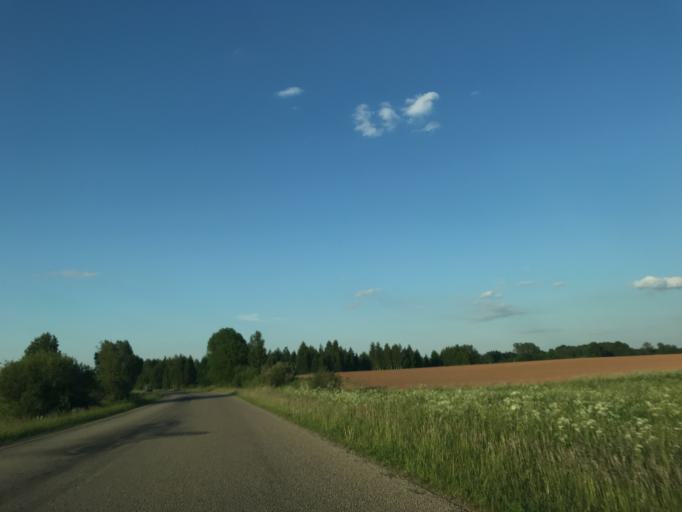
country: LV
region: Baldone
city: Baldone
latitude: 56.7083
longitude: 24.3616
